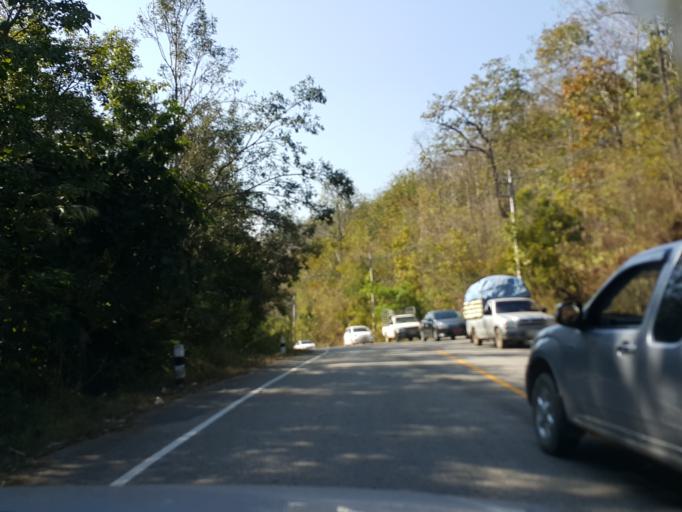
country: TH
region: Chiang Mai
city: Mae Wang
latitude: 18.6182
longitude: 98.7323
